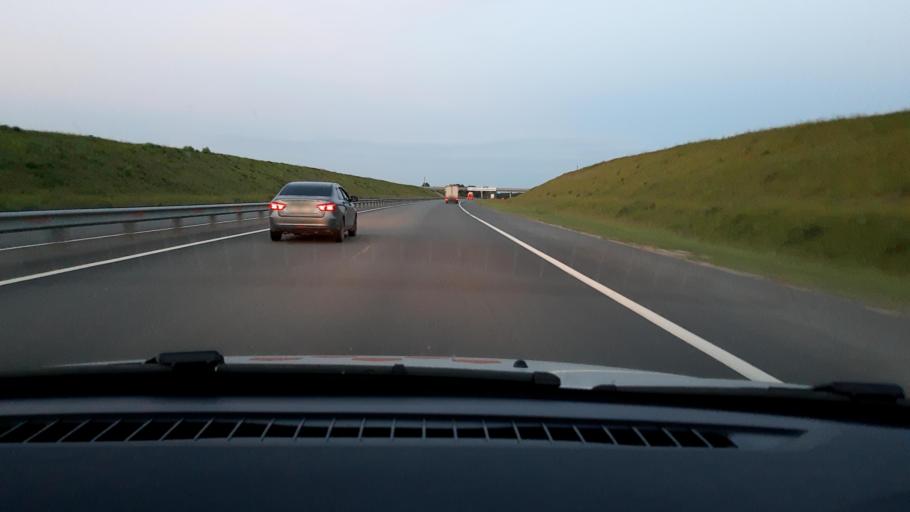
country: RU
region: Nizjnij Novgorod
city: Kstovo
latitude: 56.0954
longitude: 44.0724
